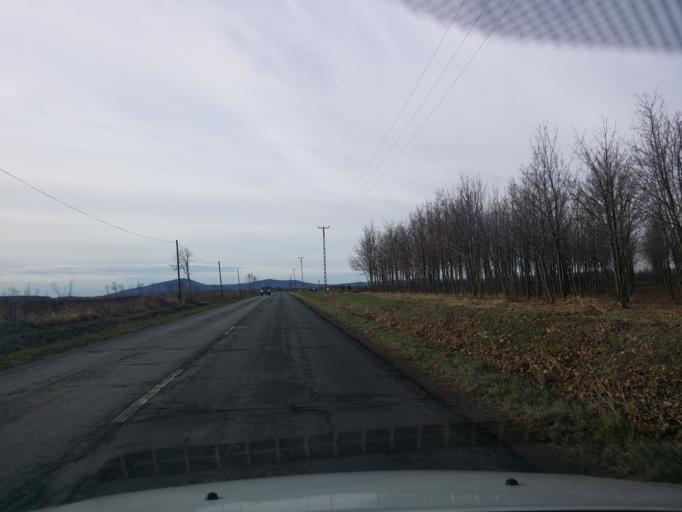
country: HU
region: Baranya
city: Boly
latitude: 45.9549
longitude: 18.4994
